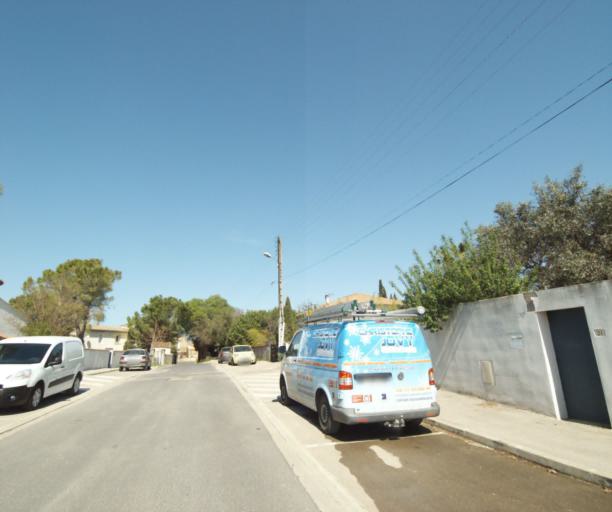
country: FR
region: Languedoc-Roussillon
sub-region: Departement de l'Herault
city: Sussargues
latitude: 43.7121
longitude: 4.0027
